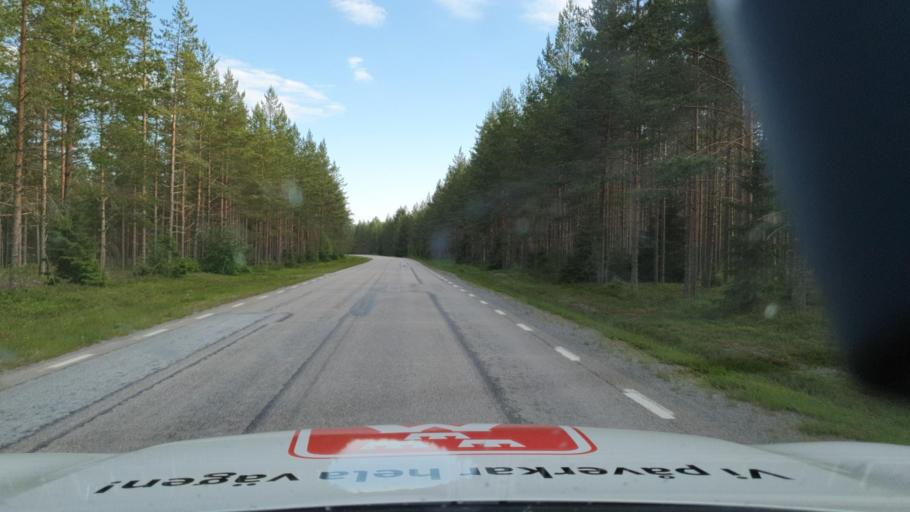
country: SE
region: Vaesterbotten
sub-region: Umea Kommun
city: Roback
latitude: 63.8660
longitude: 20.1456
